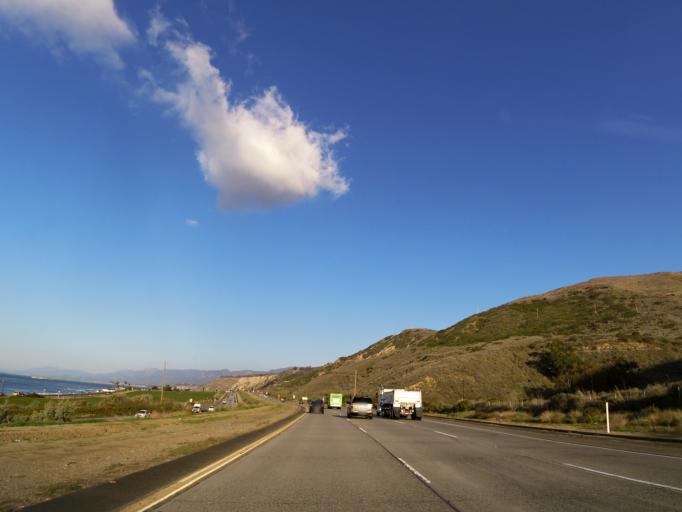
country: US
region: California
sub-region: Ventura County
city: Ventura
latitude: 34.3327
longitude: -119.4004
